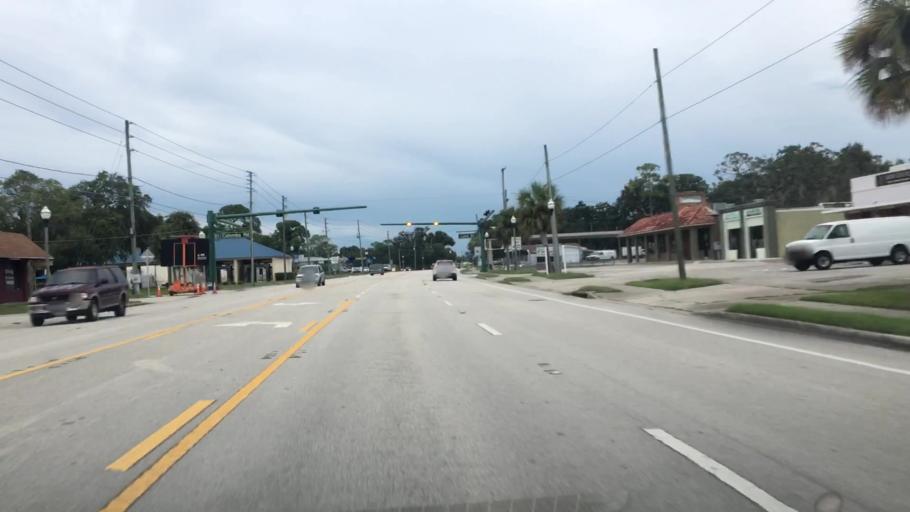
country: US
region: Florida
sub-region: Volusia County
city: DeBary
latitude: 28.8836
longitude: -81.3086
